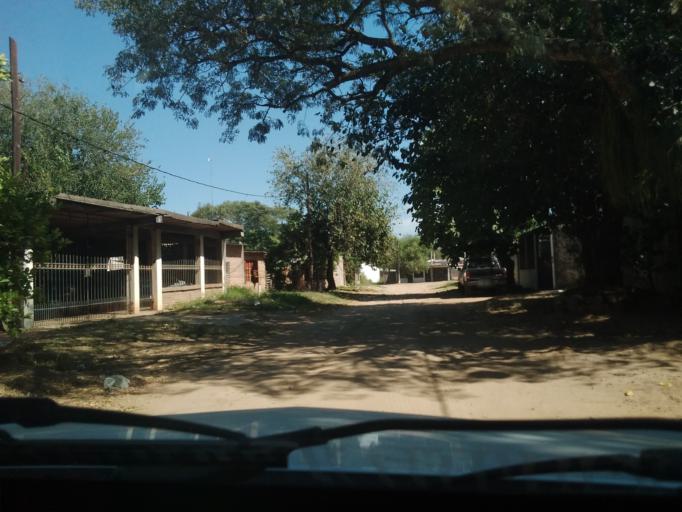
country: AR
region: Corrientes
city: Corrientes
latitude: -27.5118
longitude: -58.8066
